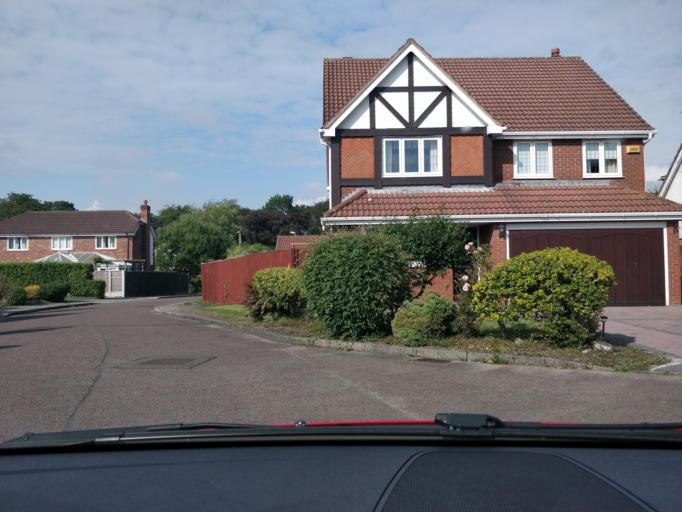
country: GB
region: England
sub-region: Sefton
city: Southport
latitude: 53.6533
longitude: -2.9601
